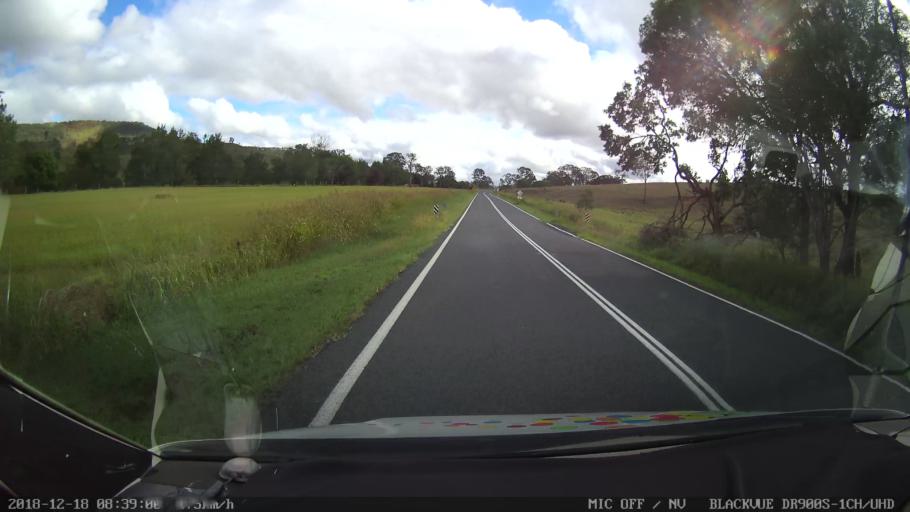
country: AU
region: New South Wales
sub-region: Kyogle
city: Kyogle
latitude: -28.2519
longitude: 152.8335
